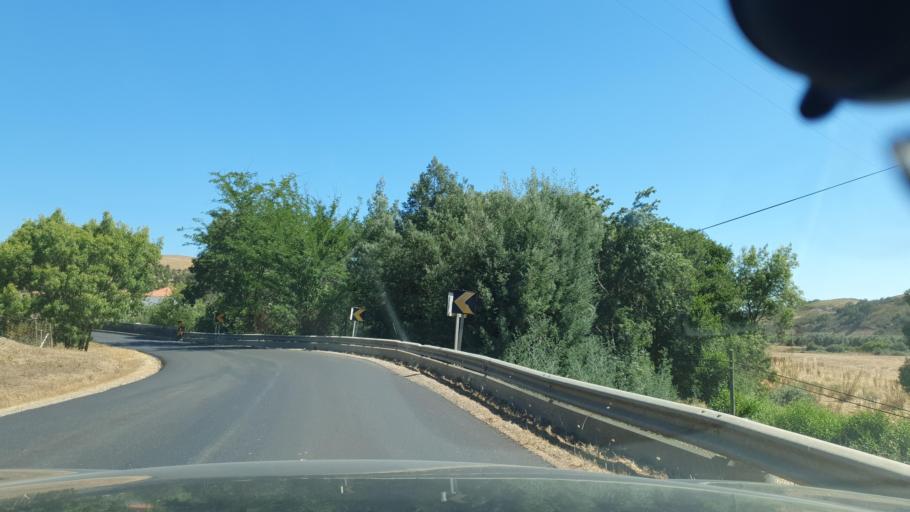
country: PT
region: Faro
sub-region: Monchique
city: Monchique
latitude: 37.4830
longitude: -8.4884
